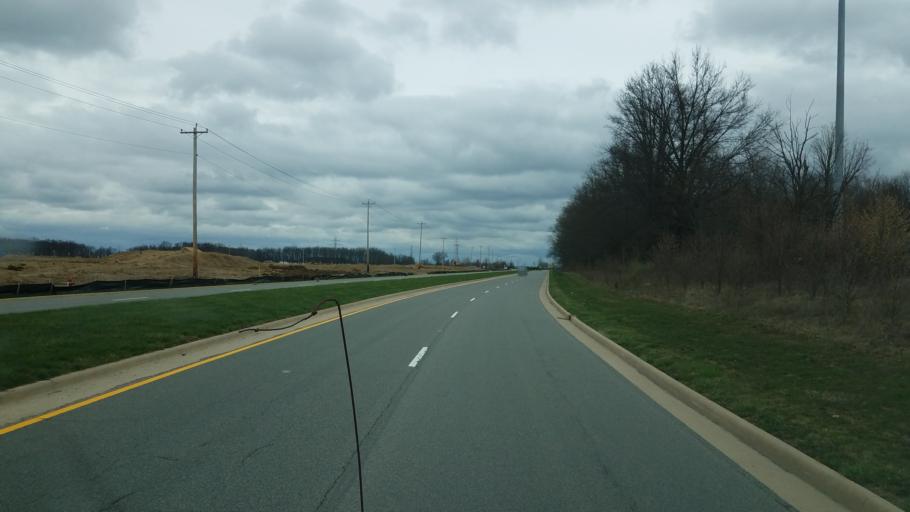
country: US
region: Ohio
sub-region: Delaware County
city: Powell
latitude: 40.2115
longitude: -83.0972
